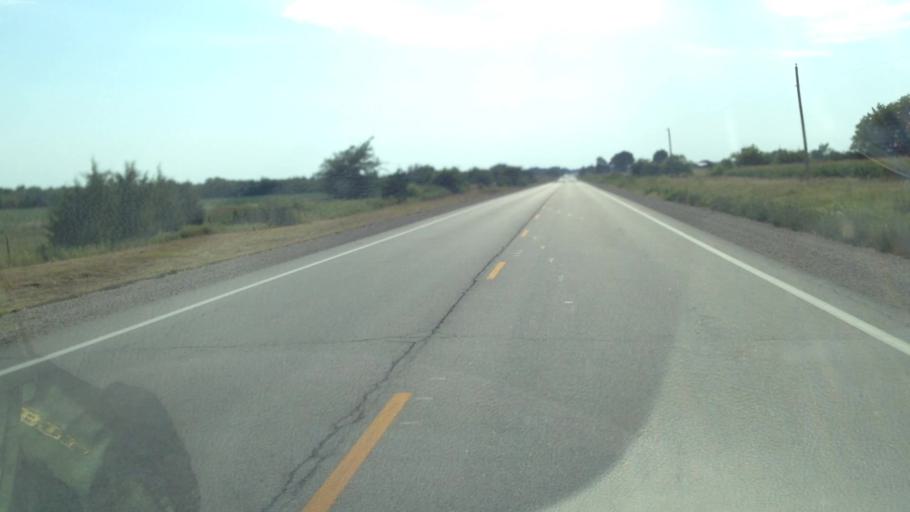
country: US
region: Kansas
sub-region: Anderson County
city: Garnett
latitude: 38.0816
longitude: -95.2183
